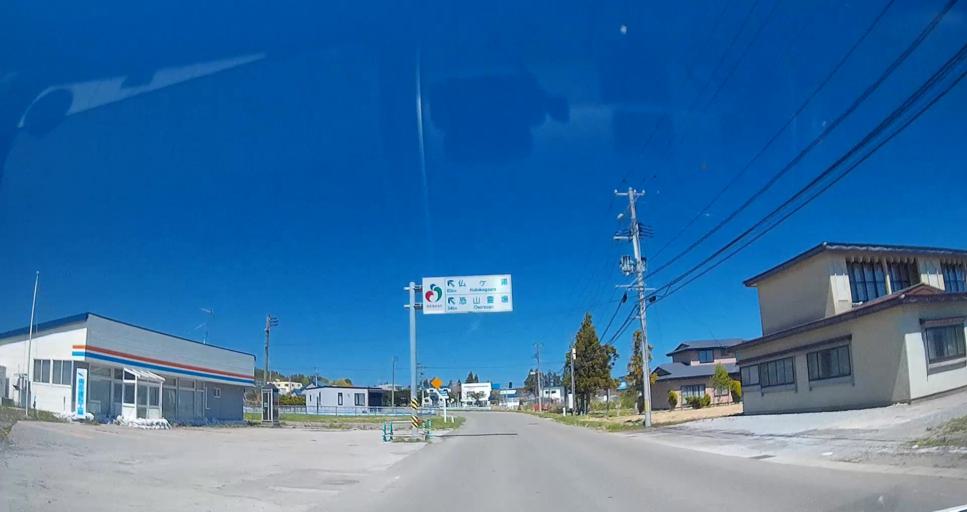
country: JP
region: Aomori
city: Mutsu
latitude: 41.2346
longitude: 141.3976
